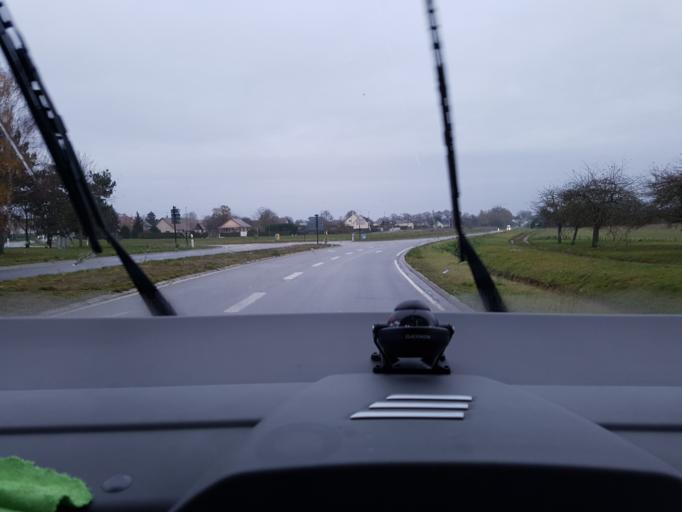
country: FR
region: Haute-Normandie
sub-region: Departement de l'Eure
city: Le Neubourg
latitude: 49.1407
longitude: 0.8910
